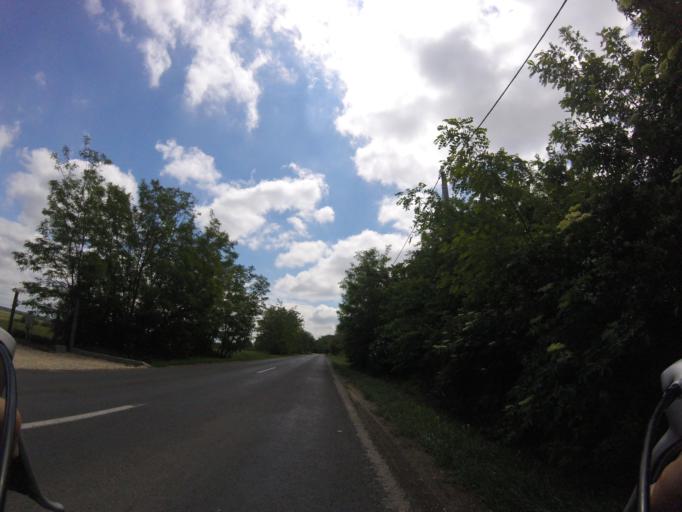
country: HU
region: Fejer
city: Seregelyes
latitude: 47.0850
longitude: 18.6009
